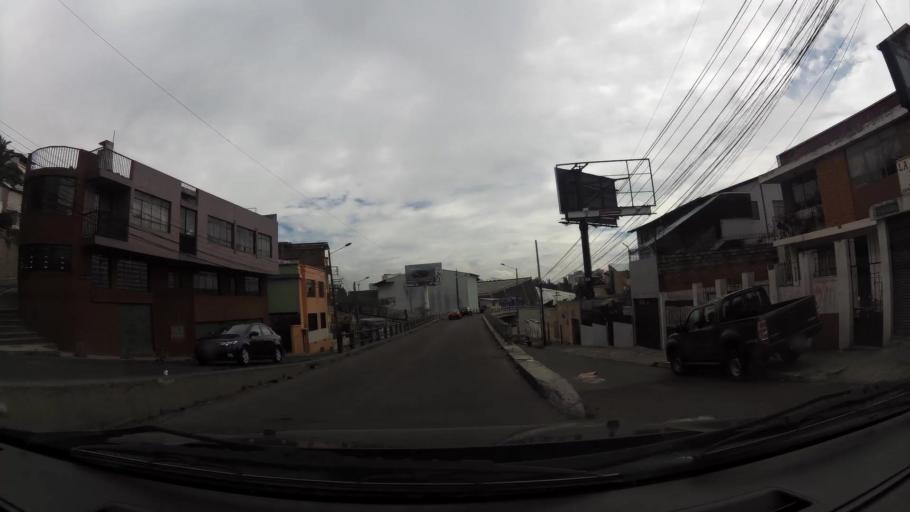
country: EC
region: Pichincha
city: Quito
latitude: -0.2162
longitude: -78.4909
